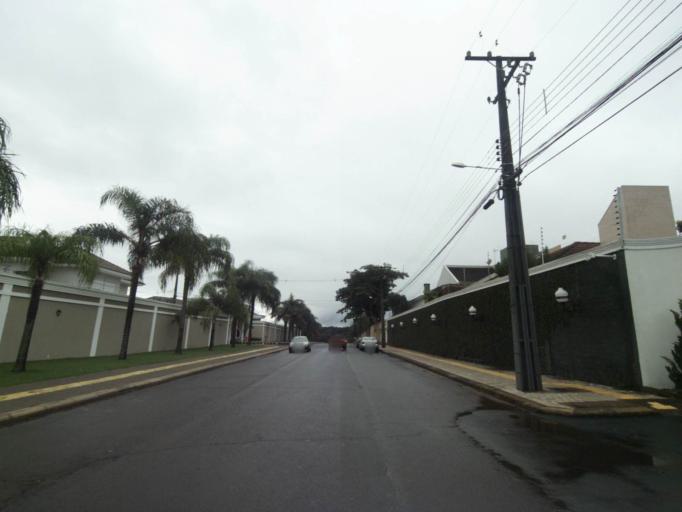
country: PY
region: Alto Parana
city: Ciudad del Este
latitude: -25.5120
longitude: -54.5805
